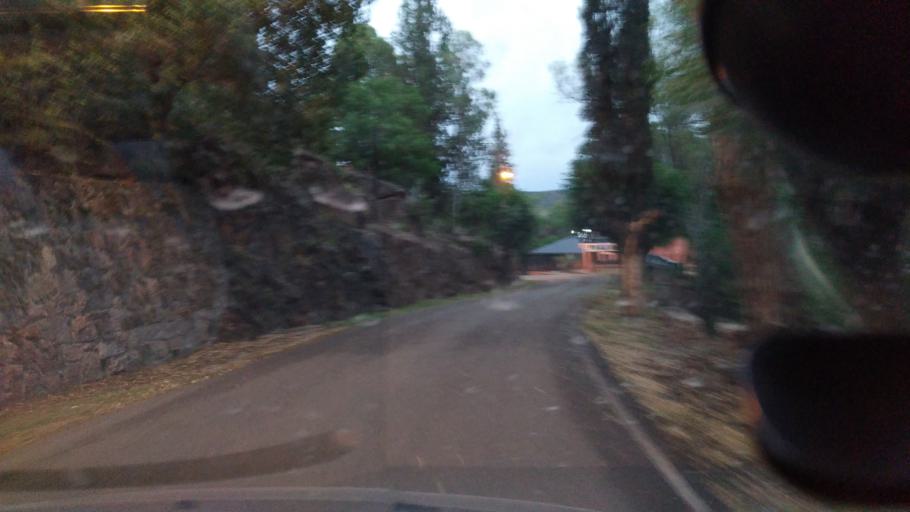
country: AR
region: Cordoba
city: Villa Las Rosas
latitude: -31.8721
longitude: -65.0325
